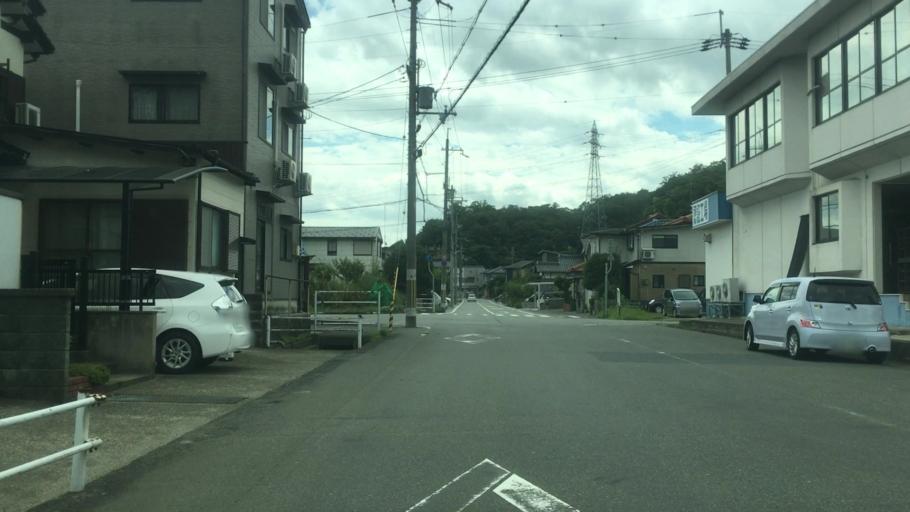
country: JP
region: Hyogo
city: Toyooka
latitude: 35.5624
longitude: 134.8033
